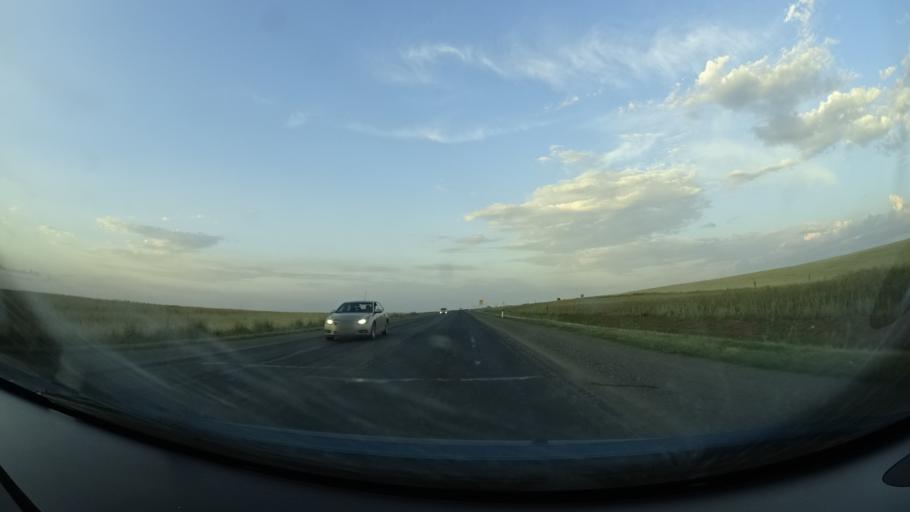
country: RU
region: Orenburg
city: Severnoye
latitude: 54.1116
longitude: 52.5118
